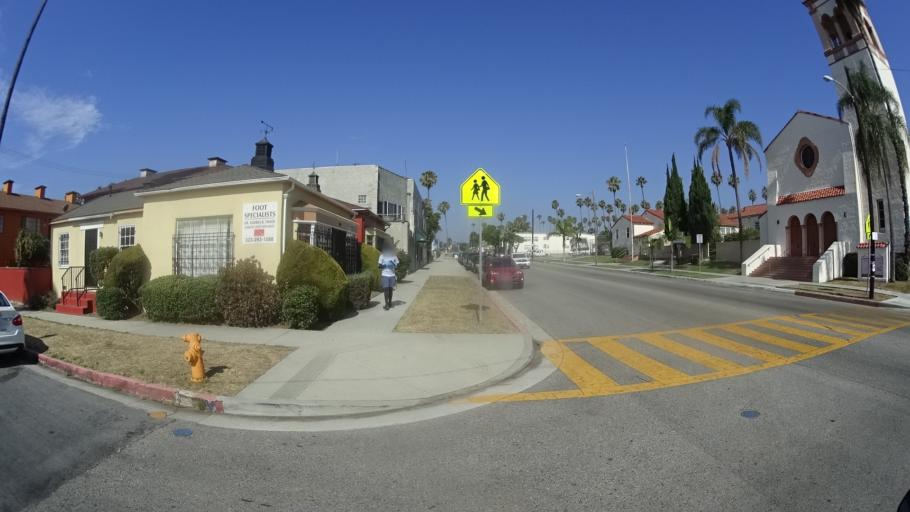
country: US
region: California
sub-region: Los Angeles County
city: View Park-Windsor Hills
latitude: 33.9930
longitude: -118.3388
